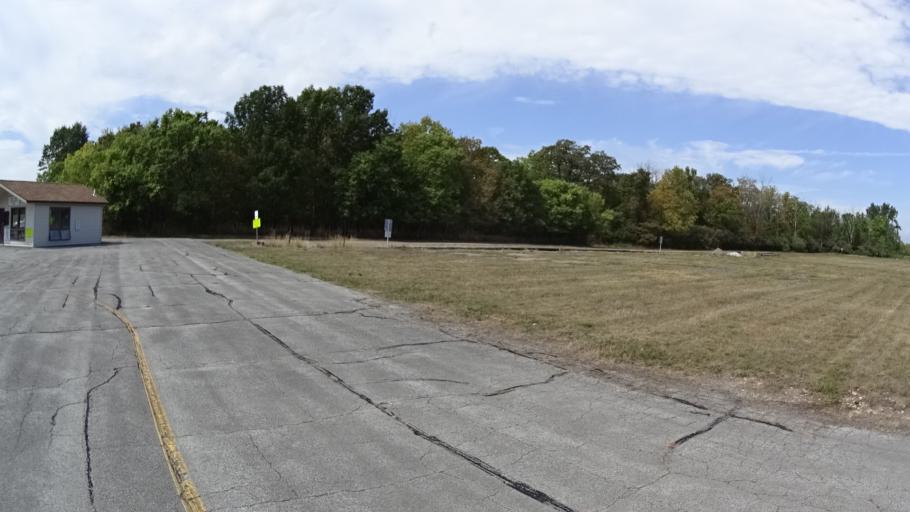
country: US
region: Ohio
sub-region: Erie County
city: Sandusky
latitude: 41.6038
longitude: -82.6874
